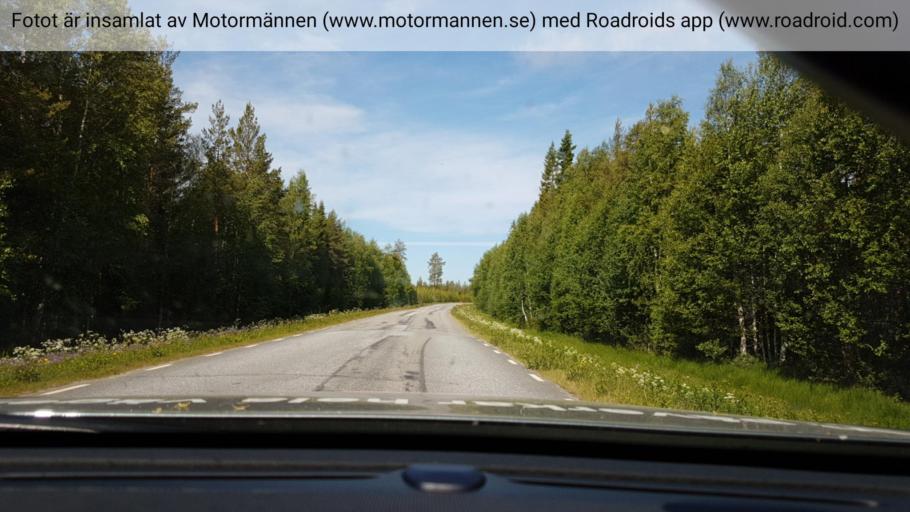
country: SE
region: Vaesterbotten
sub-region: Dorotea Kommun
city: Dorotea
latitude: 64.3673
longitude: 16.1476
